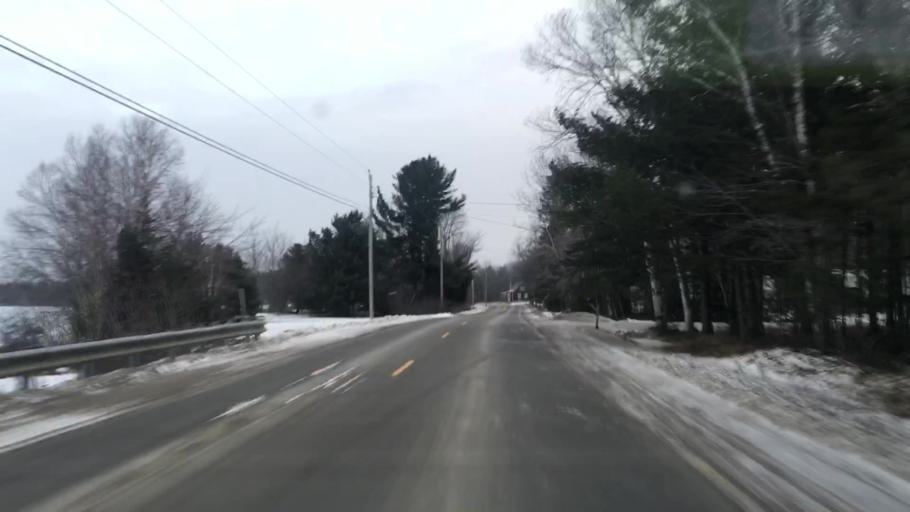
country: US
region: Maine
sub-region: Hancock County
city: Ellsworth
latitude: 44.6107
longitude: -68.3899
